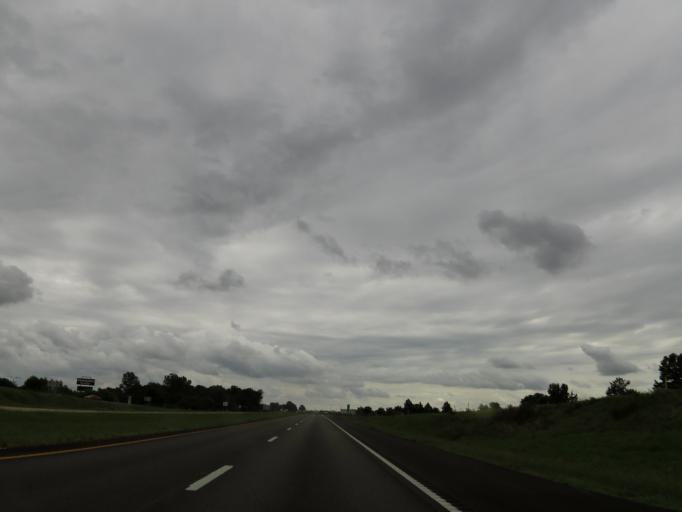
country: US
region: Missouri
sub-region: Mississippi County
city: Charleston
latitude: 36.9058
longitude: -89.3515
